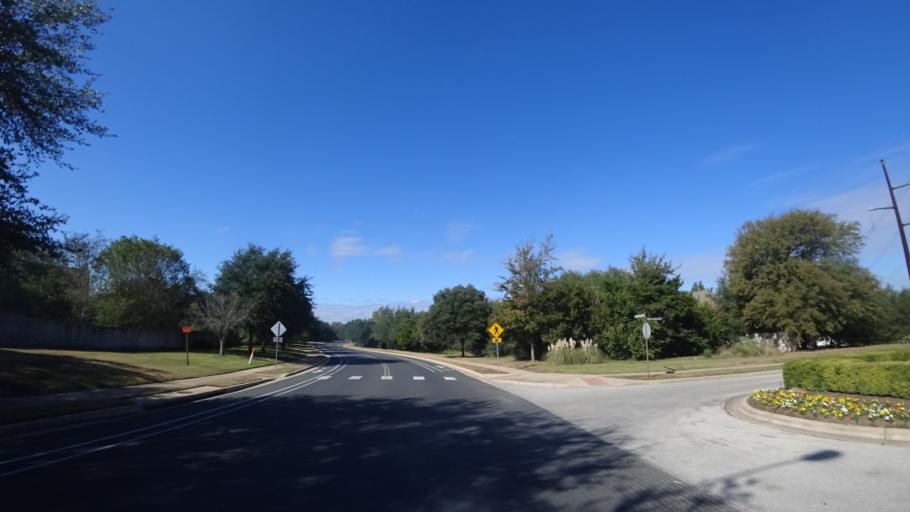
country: US
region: Texas
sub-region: Travis County
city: Hudson Bend
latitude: 30.3764
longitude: -97.8990
